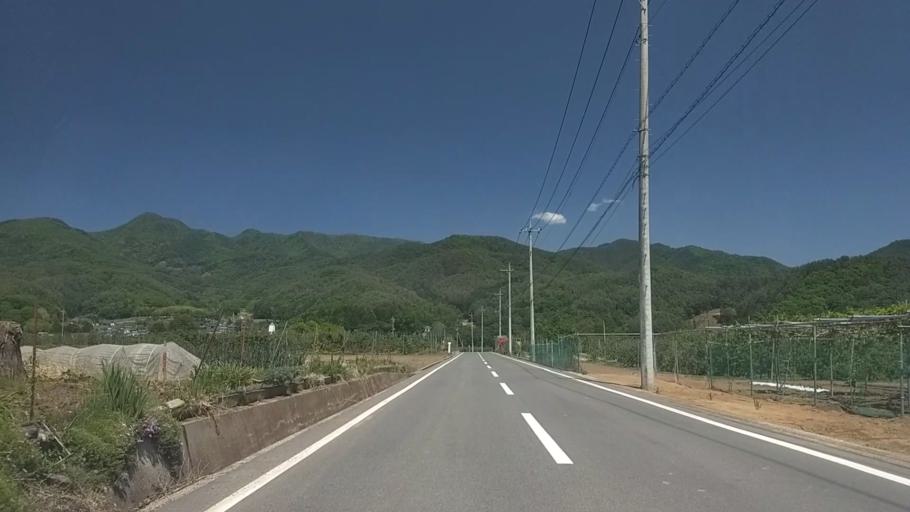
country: JP
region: Yamanashi
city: Nirasaki
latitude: 35.8499
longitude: 138.4399
